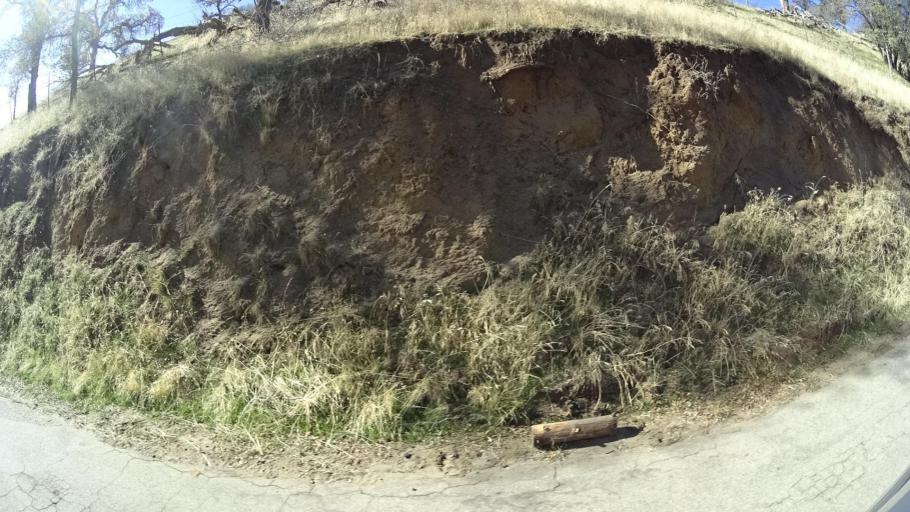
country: US
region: California
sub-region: Kern County
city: Arvin
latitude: 35.4354
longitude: -118.7293
